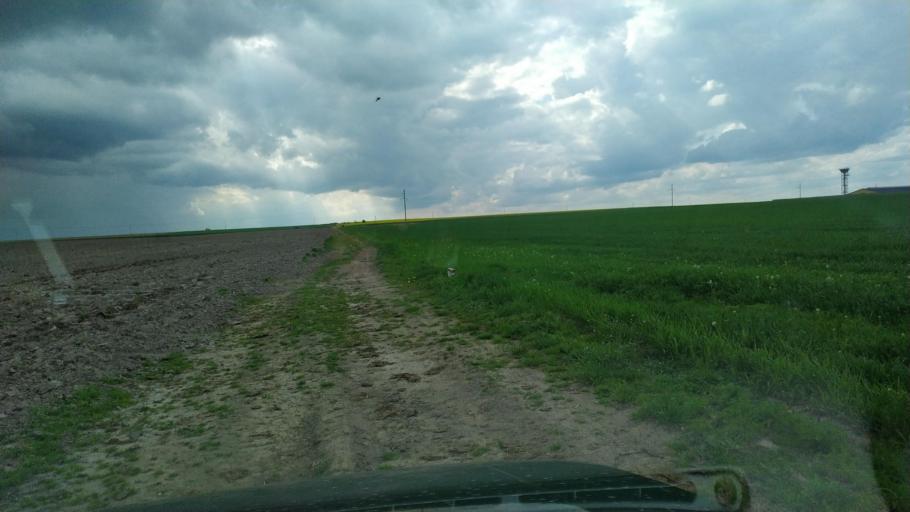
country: BY
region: Brest
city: Pruzhany
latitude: 52.6384
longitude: 24.3911
